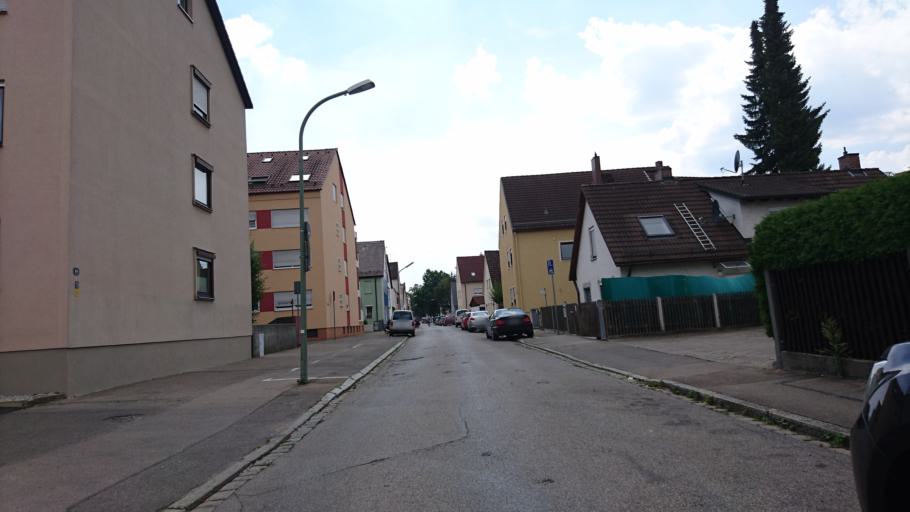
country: DE
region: Bavaria
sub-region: Swabia
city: Augsburg
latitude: 48.3792
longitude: 10.9183
